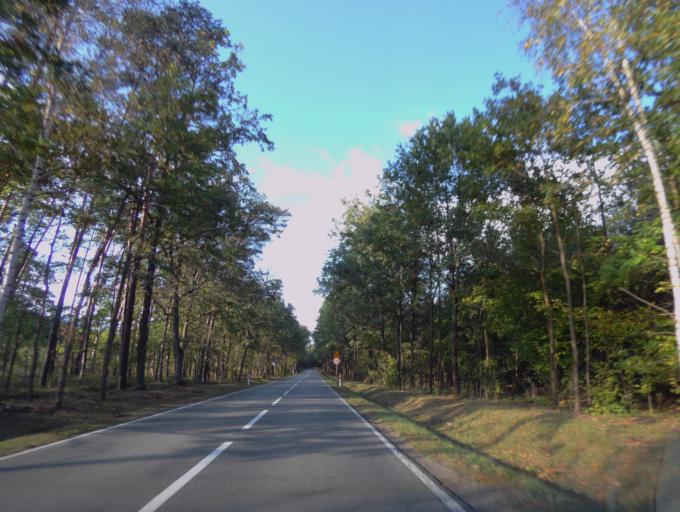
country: PL
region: Subcarpathian Voivodeship
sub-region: Powiat nizanski
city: Krzeszow
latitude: 50.3825
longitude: 22.3092
